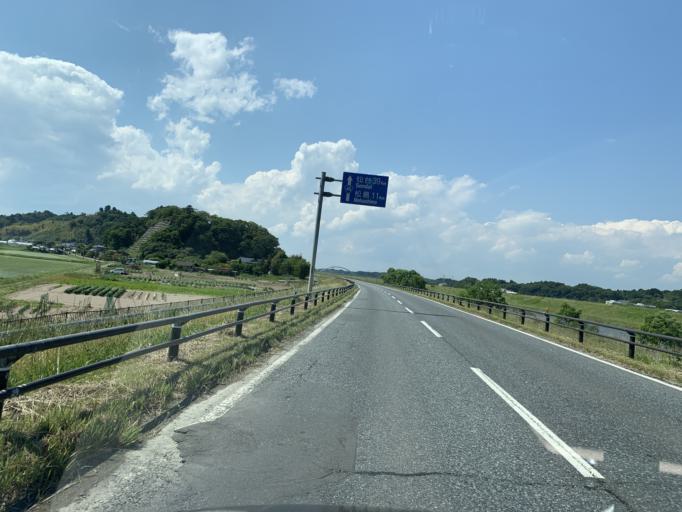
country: JP
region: Miyagi
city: Yamoto
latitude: 38.3997
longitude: 141.1539
